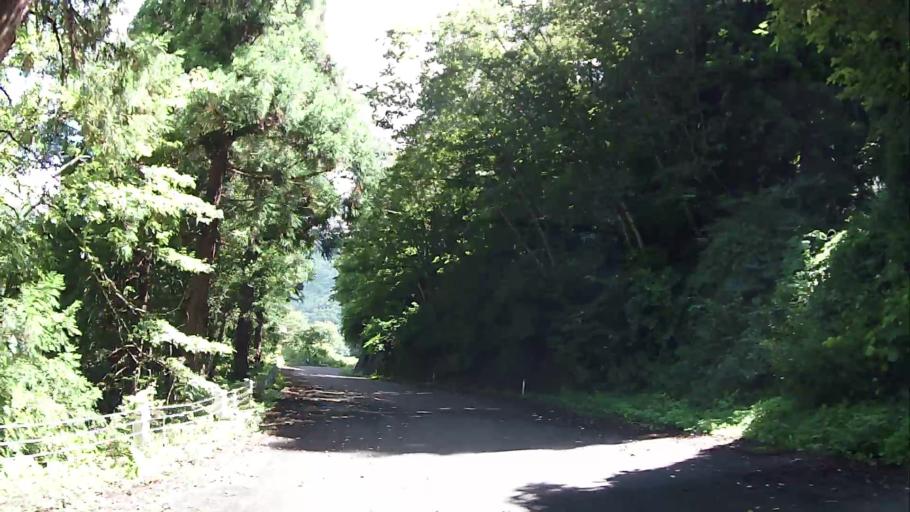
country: JP
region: Fukushima
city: Kitakata
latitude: 37.3492
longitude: 139.8674
